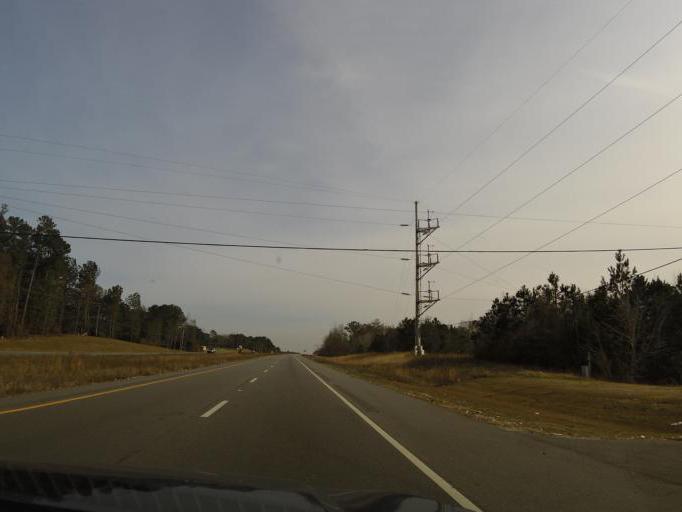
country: US
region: Alabama
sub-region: Houston County
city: Cowarts
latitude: 31.1885
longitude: -85.2815
